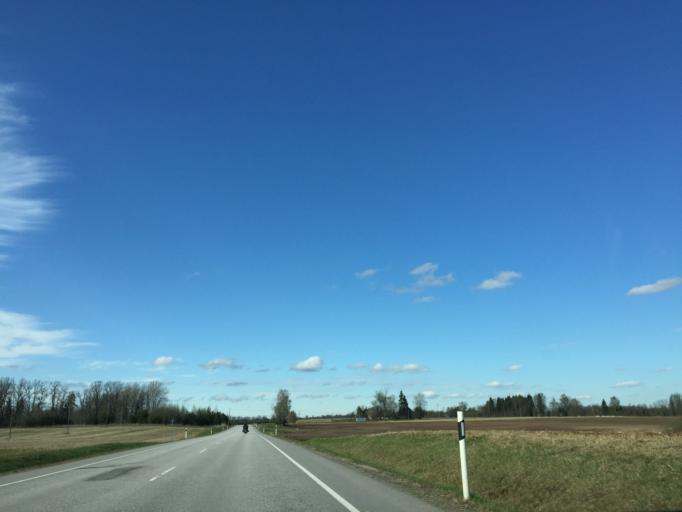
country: EE
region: Vorumaa
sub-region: Antsla vald
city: Vana-Antsla
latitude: 57.8930
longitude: 26.2888
